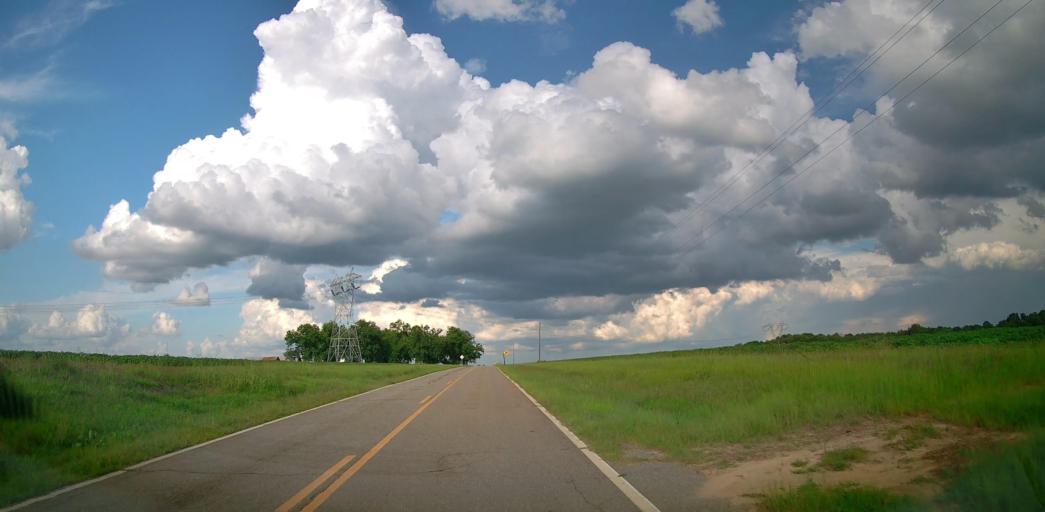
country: US
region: Georgia
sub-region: Bleckley County
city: Cochran
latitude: 32.4064
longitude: -83.4130
